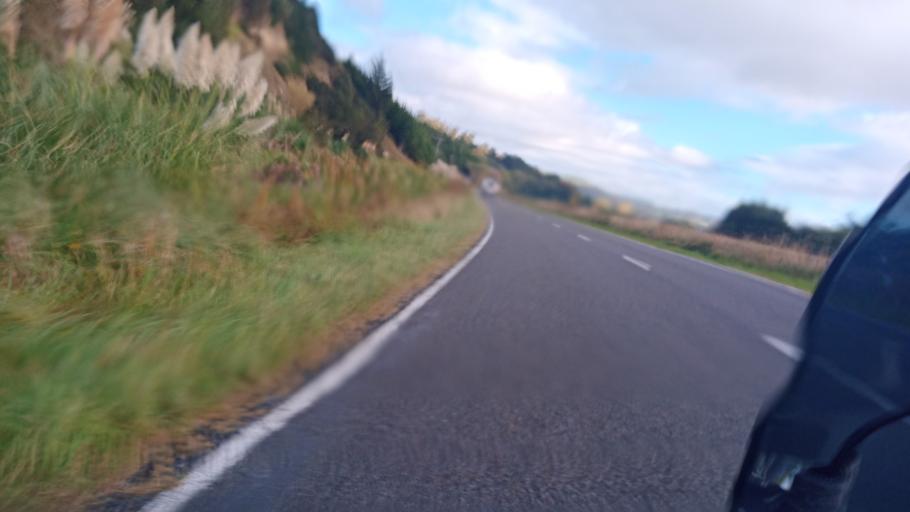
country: NZ
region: Gisborne
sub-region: Gisborne District
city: Gisborne
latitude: -38.6058
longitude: 177.8101
